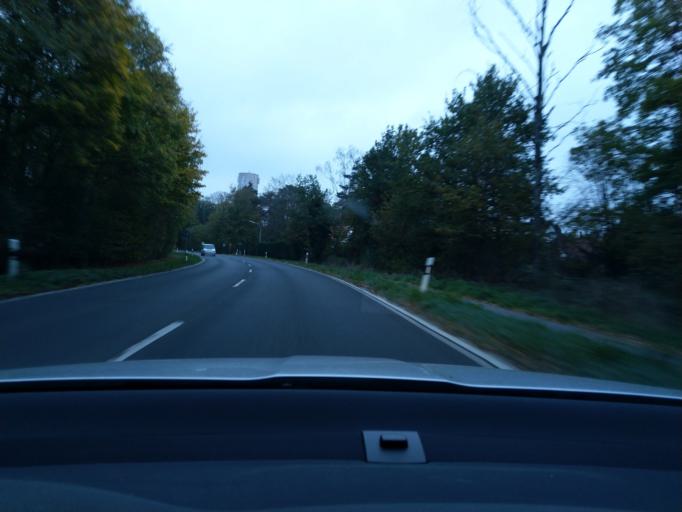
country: DE
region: North Rhine-Westphalia
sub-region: Regierungsbezirk Dusseldorf
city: Schwalmtal
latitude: 51.2037
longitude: 6.2994
